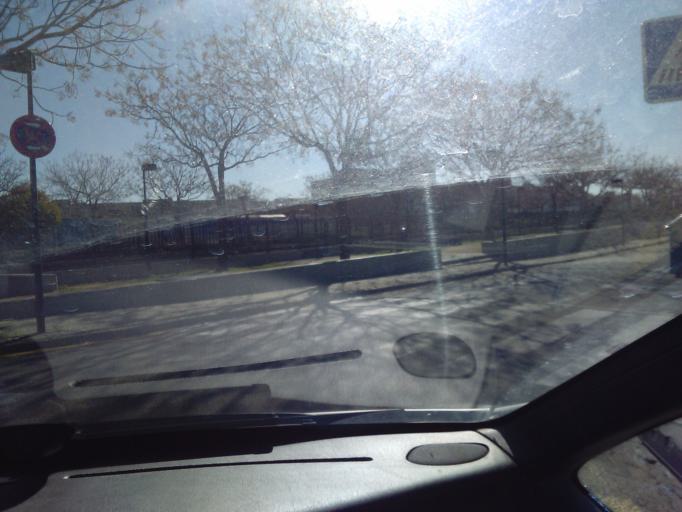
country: ES
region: Andalusia
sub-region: Provincia de Sevilla
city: Sevilla
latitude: 37.3903
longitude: -5.9068
